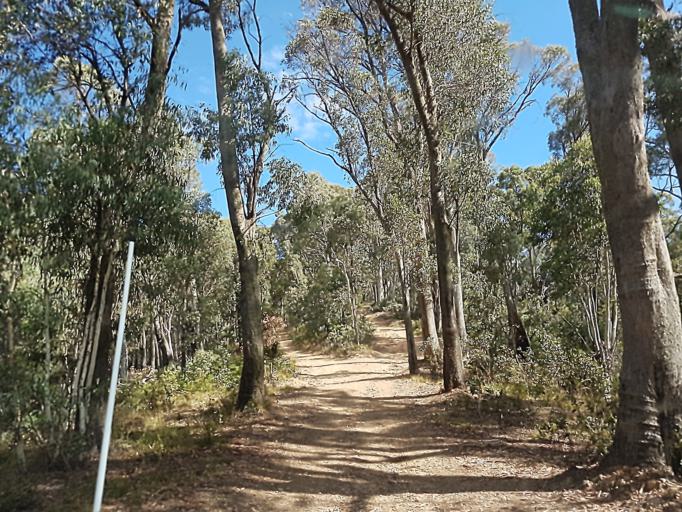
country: AU
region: Victoria
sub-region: Alpine
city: Mount Beauty
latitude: -36.9275
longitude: 146.9945
